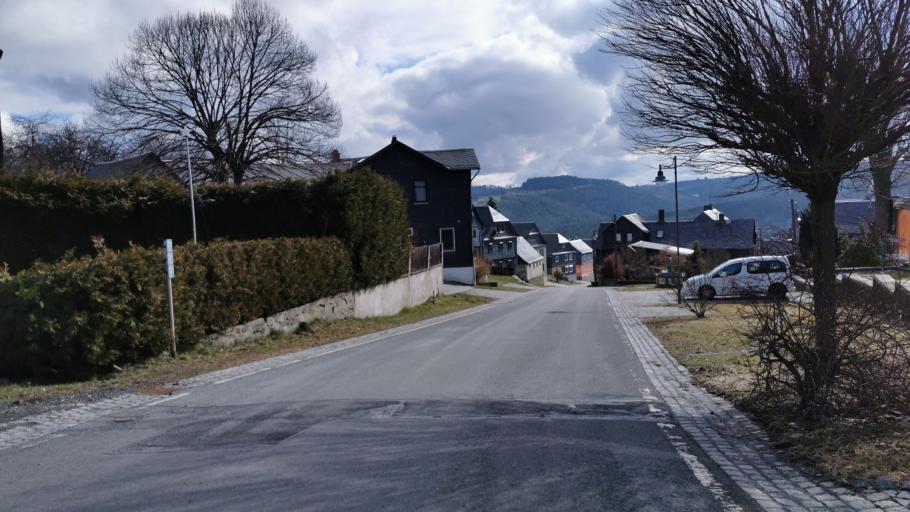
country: DE
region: Thuringia
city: Wurzbach
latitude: 50.4938
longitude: 11.4766
